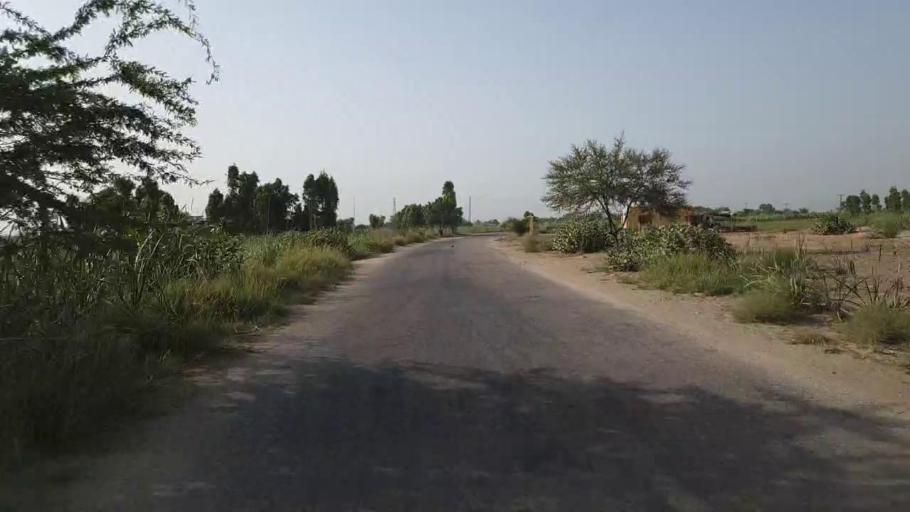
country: PK
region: Sindh
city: Jam Sahib
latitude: 26.4190
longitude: 68.8704
